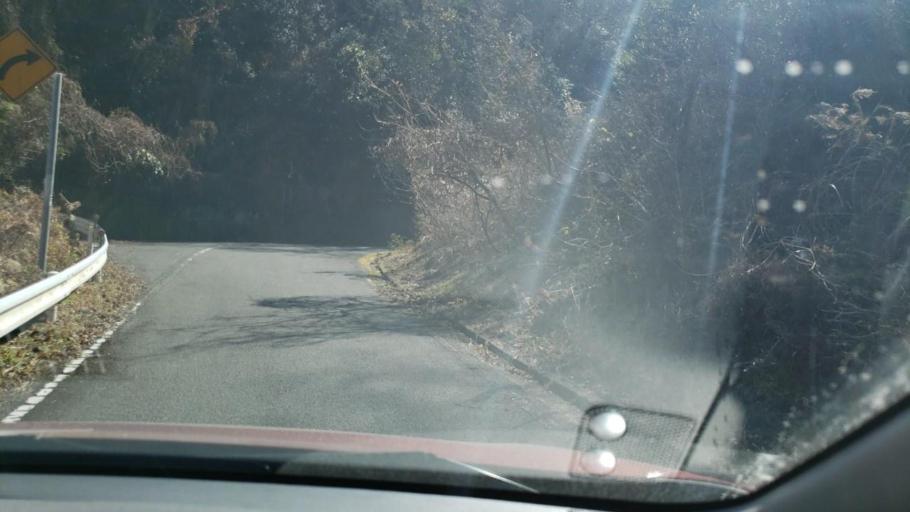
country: JP
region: Tokushima
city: Narutocho-mitsuishi
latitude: 34.1977
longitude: 134.5536
